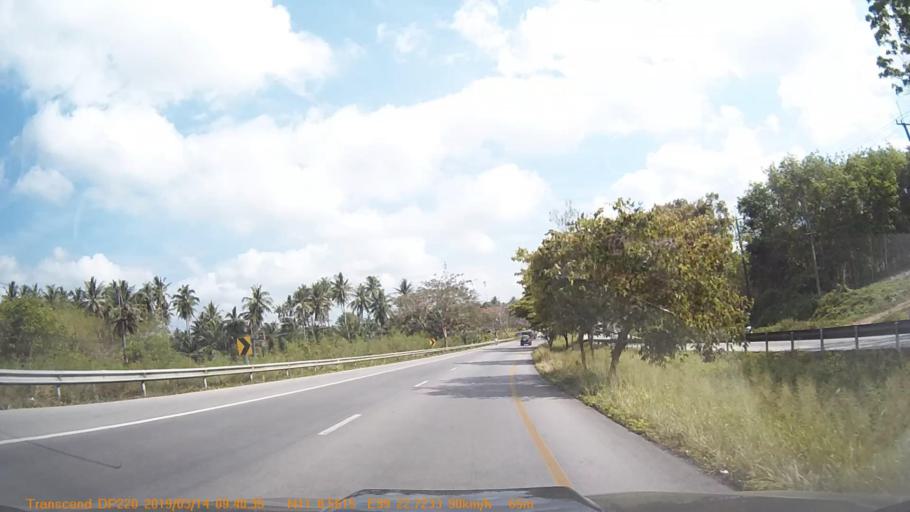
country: TH
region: Prachuap Khiri Khan
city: Bang Saphan Noi
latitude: 11.1429
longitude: 99.3788
